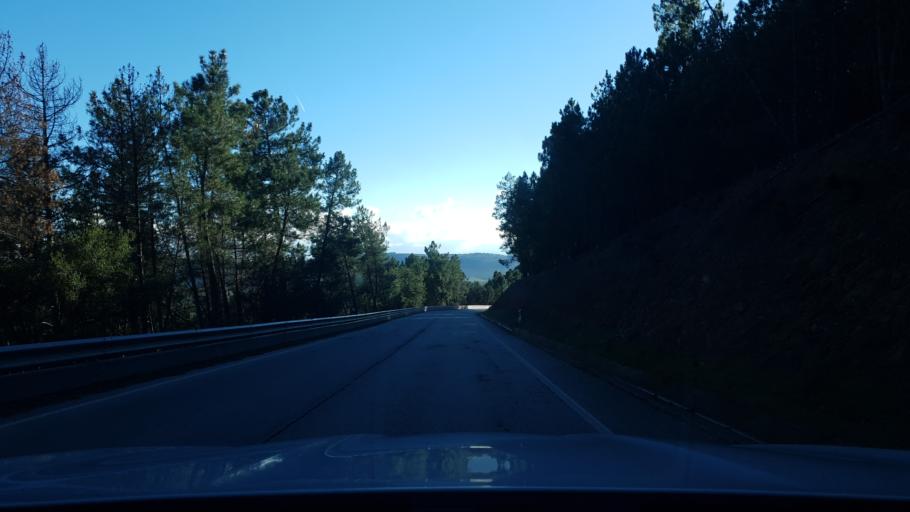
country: PT
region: Braganca
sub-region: Freixo de Espada A Cinta
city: Freixo de Espada a Cinta
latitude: 41.1071
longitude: -6.8271
